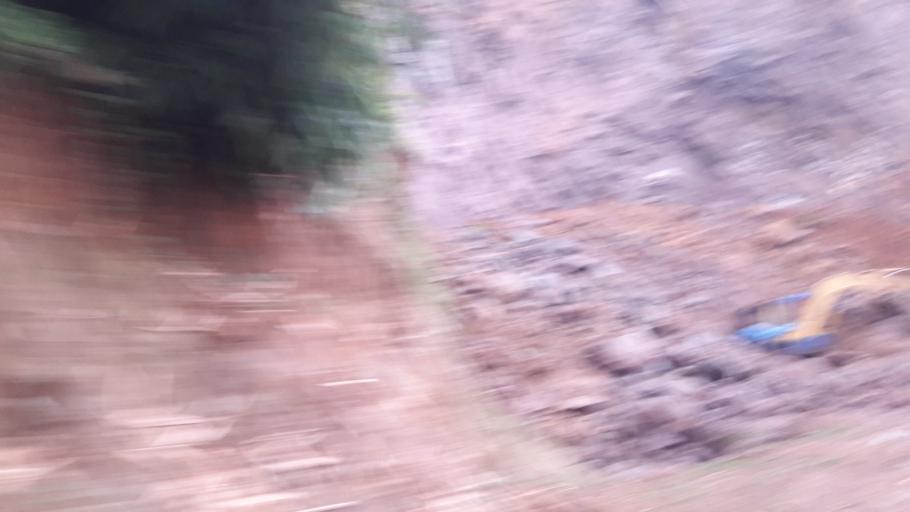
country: ID
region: West Java
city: Cipeundeuy
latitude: -6.6528
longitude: 106.5195
